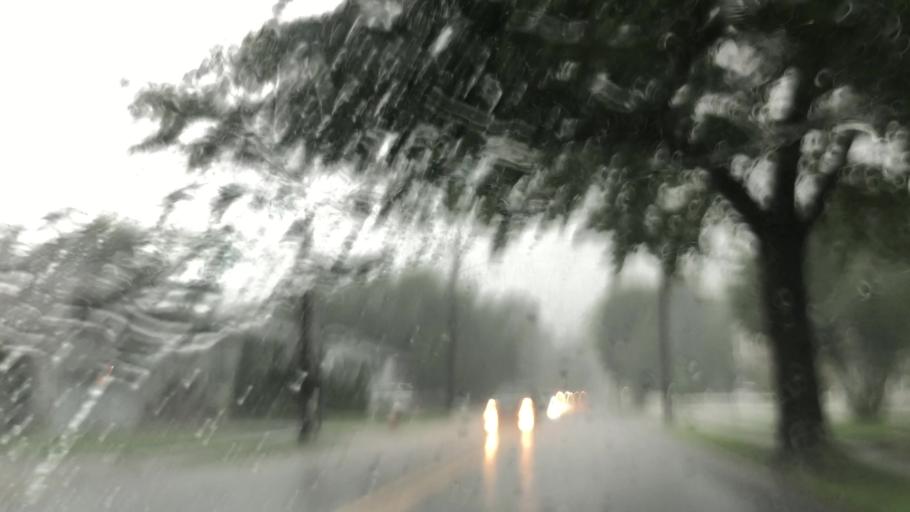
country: US
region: New Jersey
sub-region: Bergen County
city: Rochelle Park
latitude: 40.8971
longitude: -74.0786
